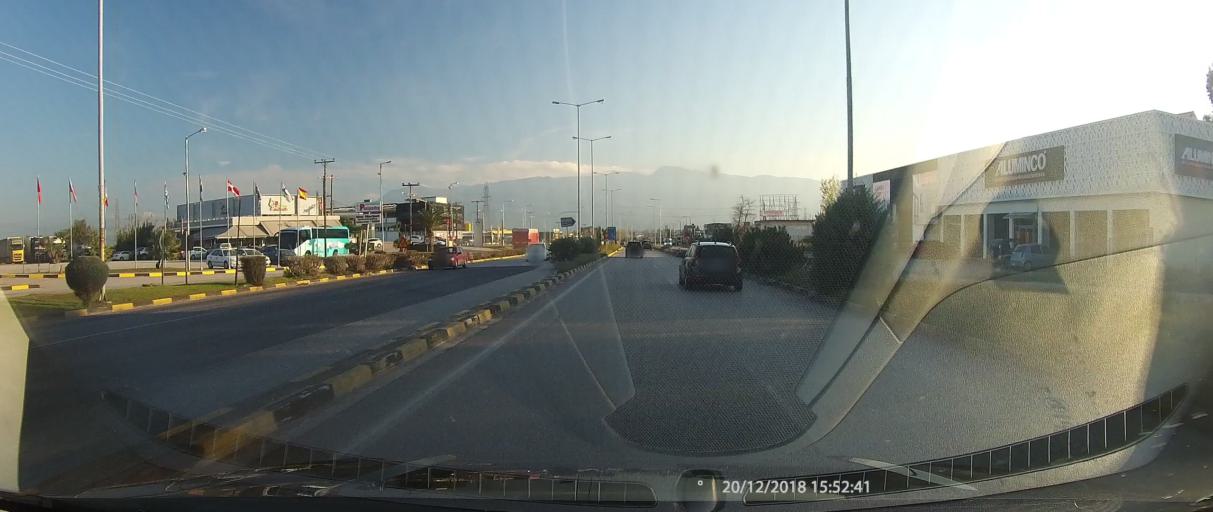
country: GR
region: Central Greece
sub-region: Nomos Fthiotidos
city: Rodhitsa
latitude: 38.8793
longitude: 22.4531
